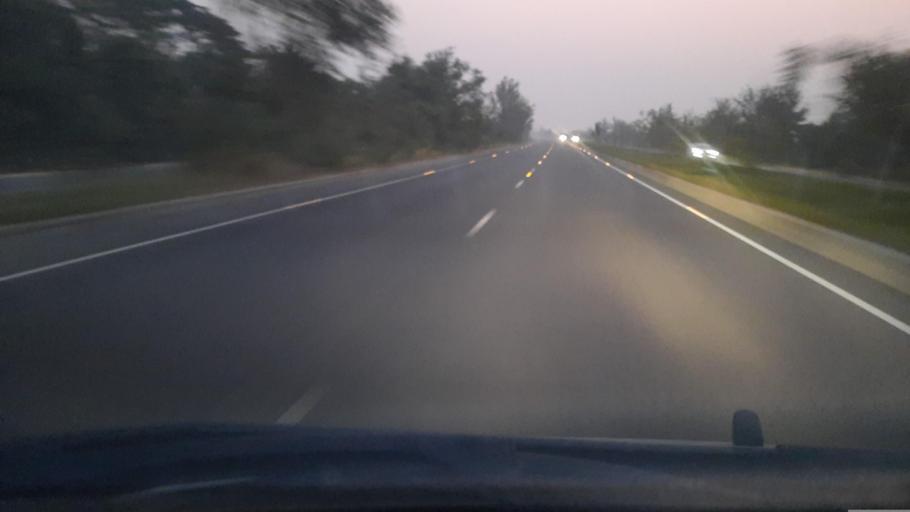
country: BD
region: Dhaka
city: Char Bhadrasan
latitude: 23.3980
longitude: 90.2259
